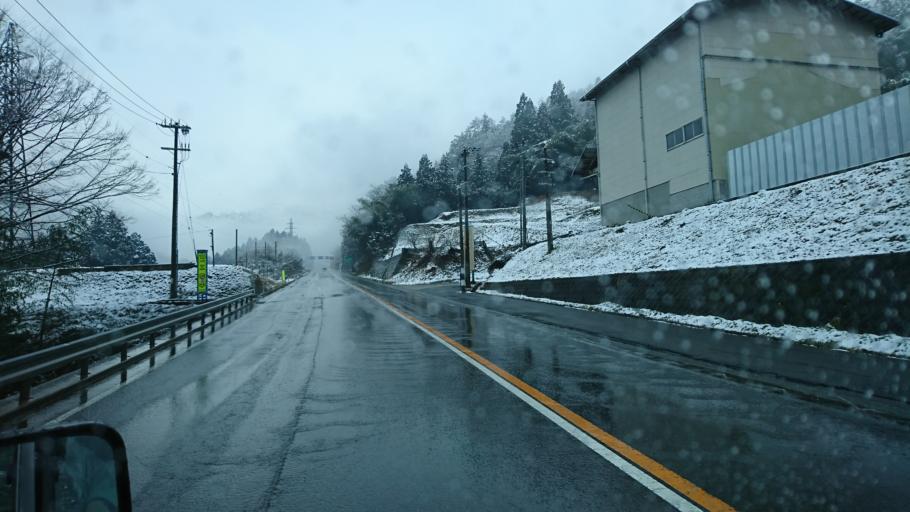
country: JP
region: Hyogo
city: Toyooka
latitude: 35.4906
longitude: 134.5486
